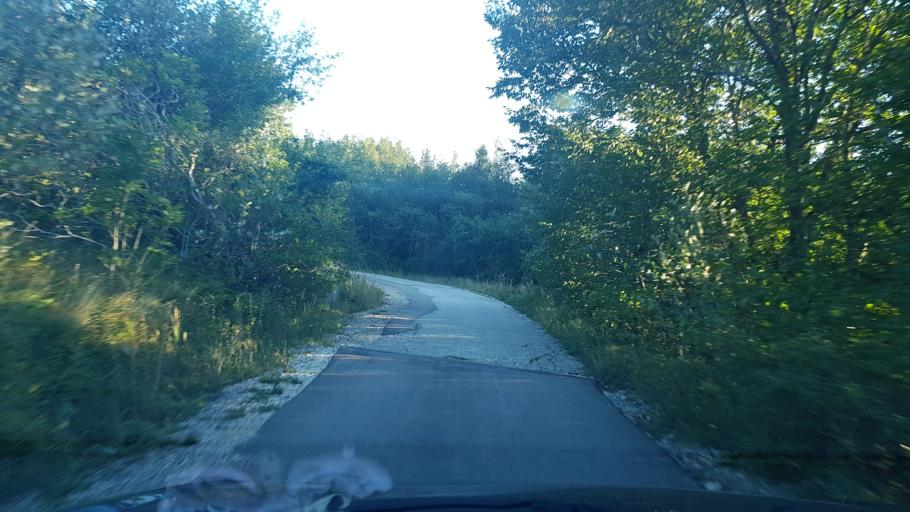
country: SI
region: Vipava
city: Vipava
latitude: 45.7866
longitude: 14.0253
